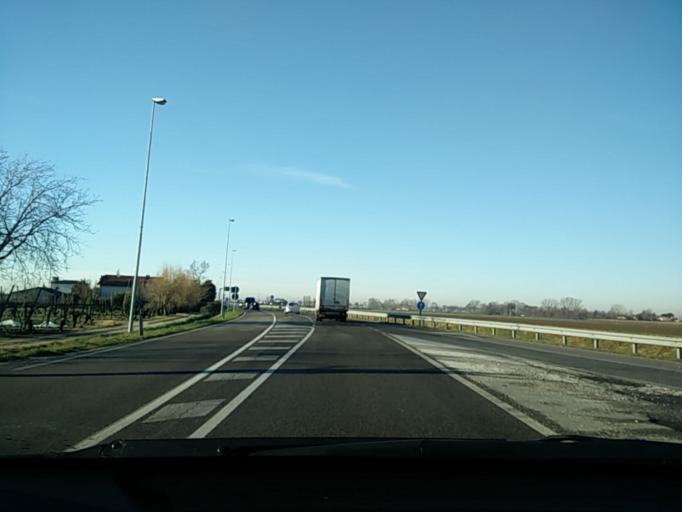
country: IT
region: Veneto
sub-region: Provincia di Venezia
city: Fossalta di Piave
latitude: 45.6191
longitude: 12.4960
